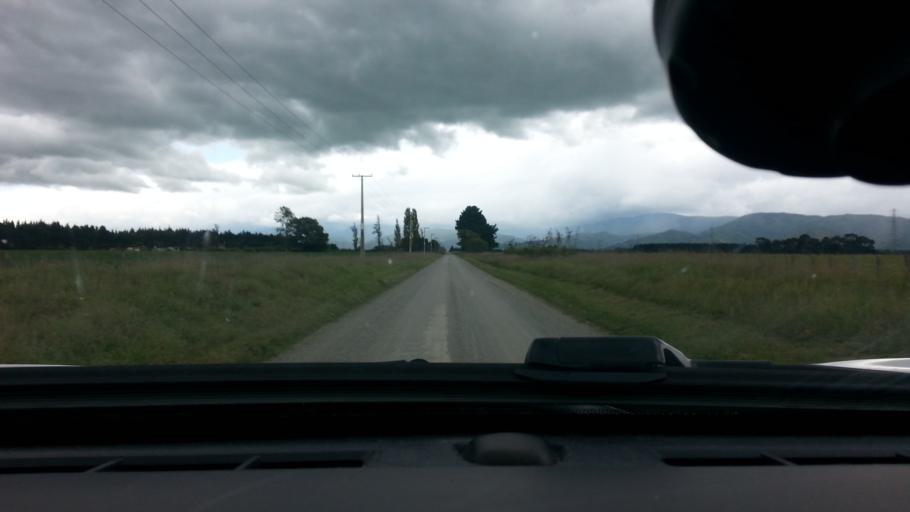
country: NZ
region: Wellington
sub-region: Masterton District
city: Masterton
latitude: -41.1190
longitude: 175.4183
